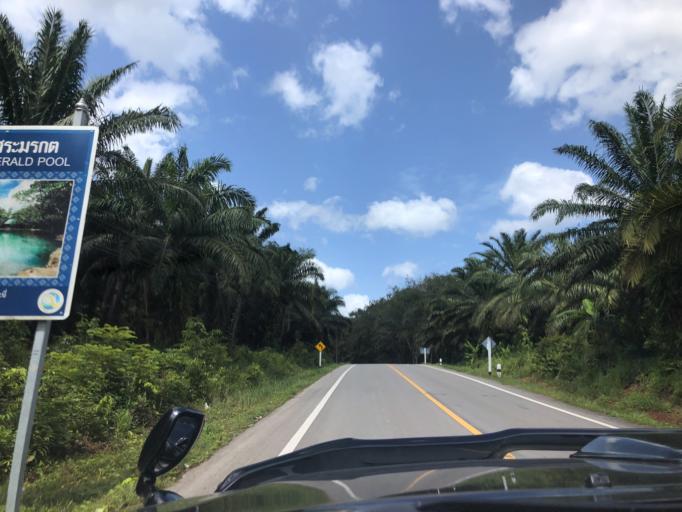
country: TH
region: Krabi
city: Khlong Thom
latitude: 7.9464
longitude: 99.2116
